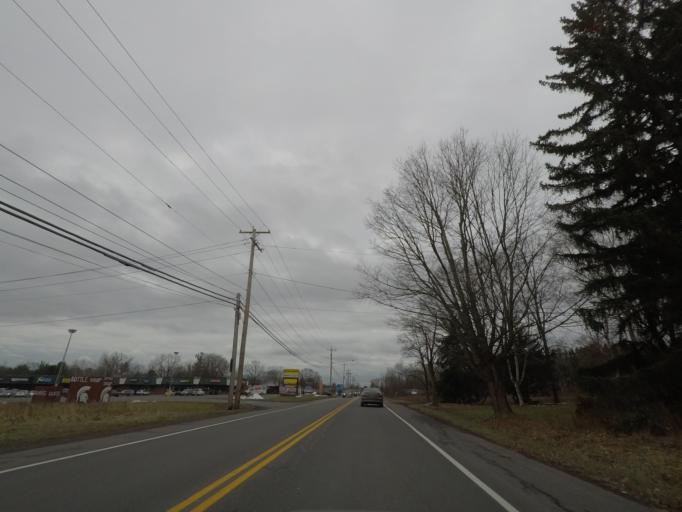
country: US
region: New York
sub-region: Schenectady County
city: East Glenville
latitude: 42.9059
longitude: -73.9020
